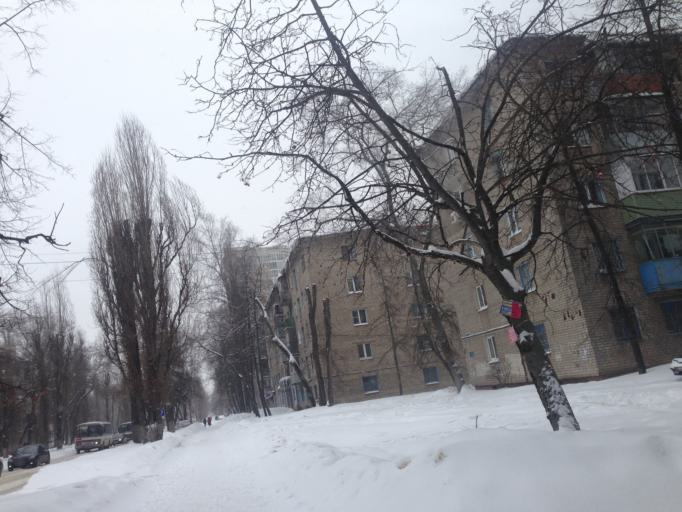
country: RU
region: Voronezj
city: Voronezh
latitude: 51.6548
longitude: 39.1498
